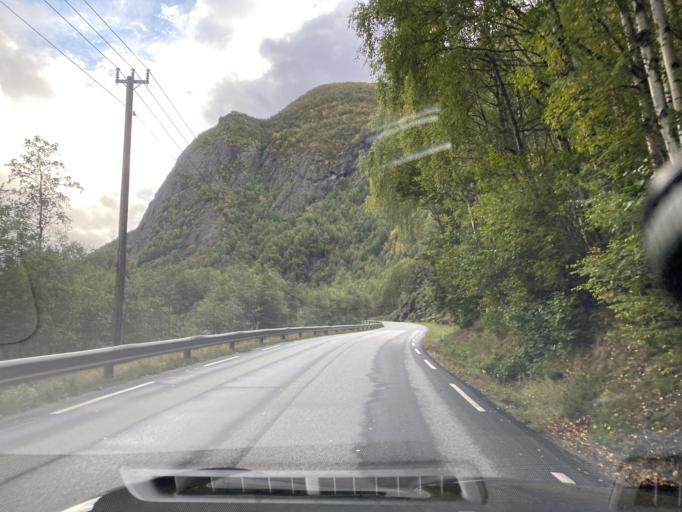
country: NO
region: Oppland
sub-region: Lom
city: Fossbergom
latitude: 61.7819
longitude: 8.4341
